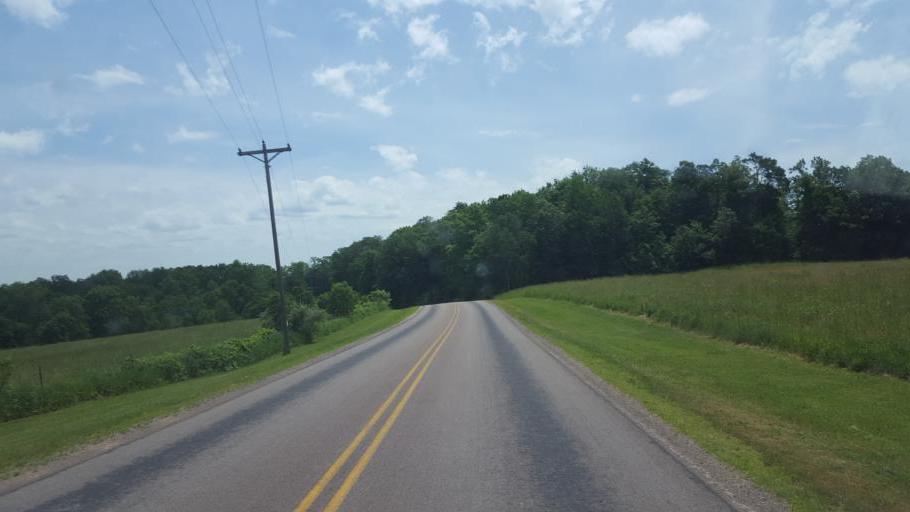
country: US
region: Wisconsin
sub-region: Vernon County
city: Hillsboro
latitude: 43.5914
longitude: -90.3862
